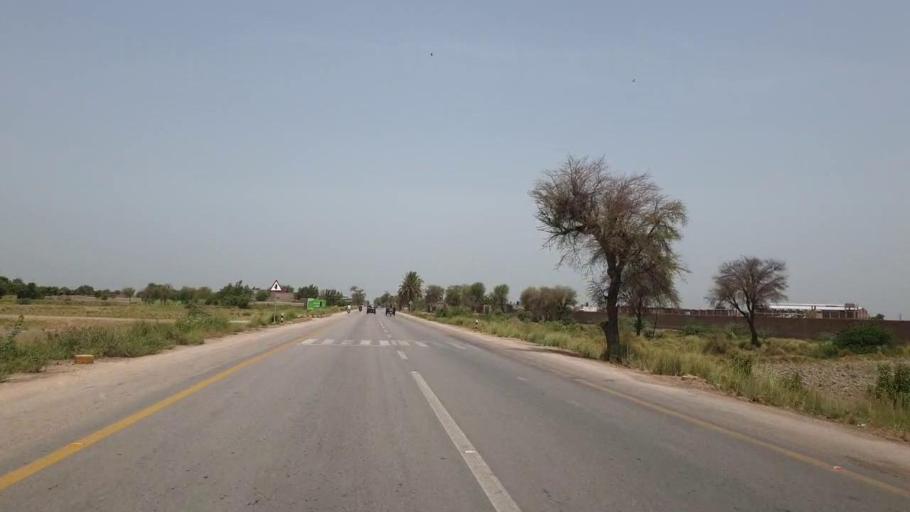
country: PK
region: Sindh
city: Nawabshah
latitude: 26.2149
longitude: 68.5083
